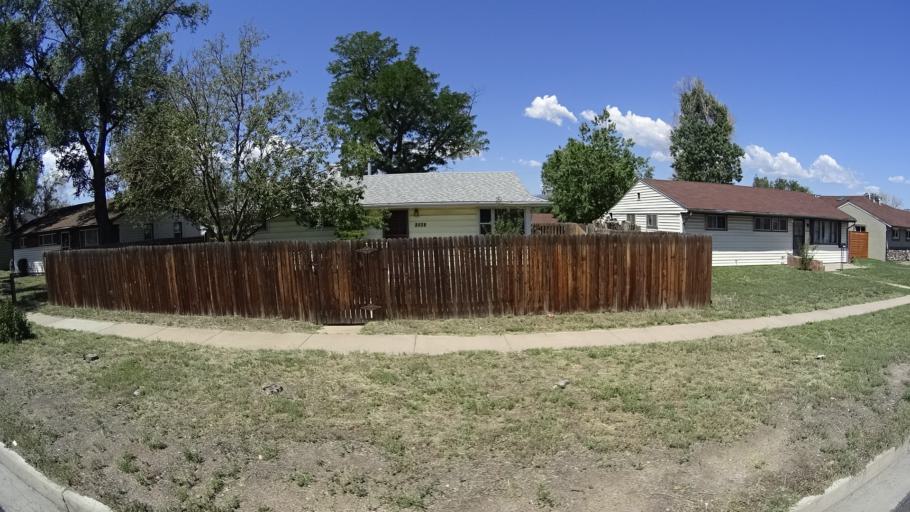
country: US
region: Colorado
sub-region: El Paso County
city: Colorado Springs
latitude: 38.8690
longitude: -104.7942
